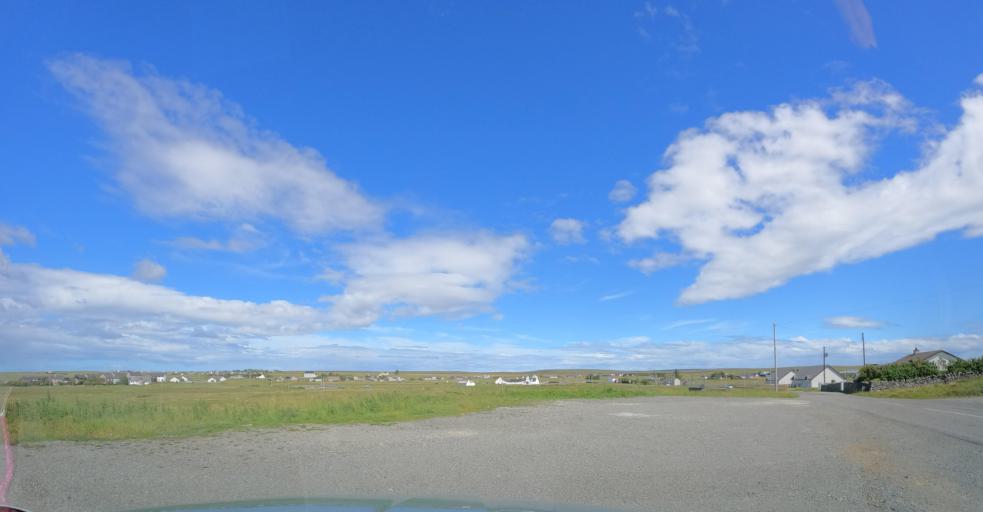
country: GB
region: Scotland
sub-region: Eilean Siar
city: Isle of Lewis
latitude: 58.3491
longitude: -6.5264
